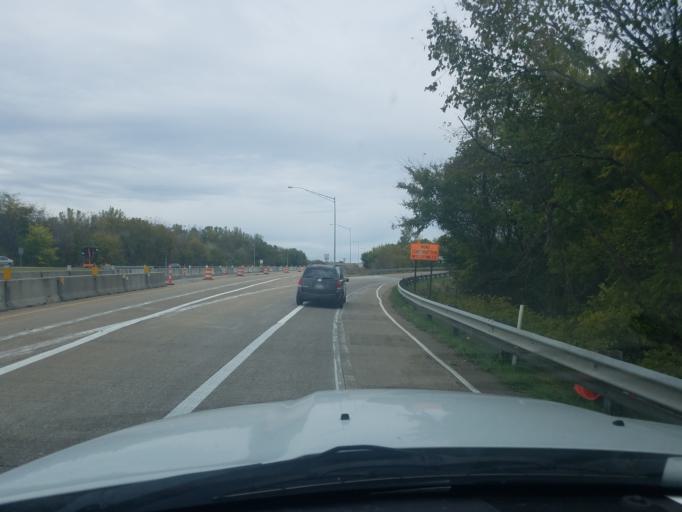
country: US
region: Indiana
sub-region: Vanderburgh County
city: Evansville
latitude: 37.9343
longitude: -87.5475
